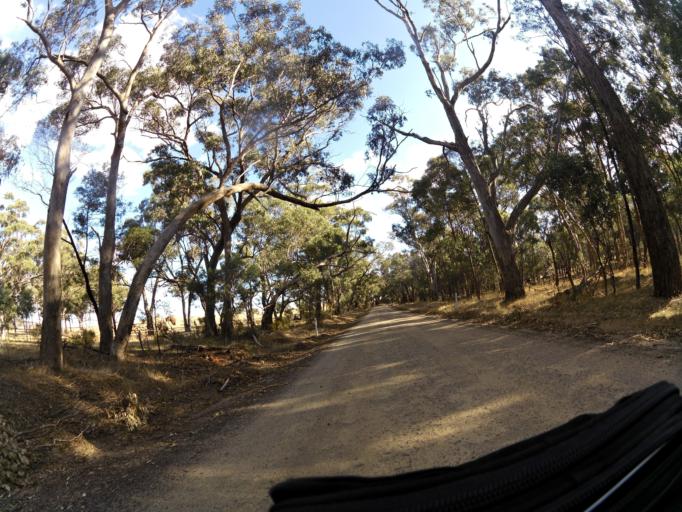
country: AU
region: Victoria
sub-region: Greater Bendigo
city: Kennington
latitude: -37.0189
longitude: 144.8056
